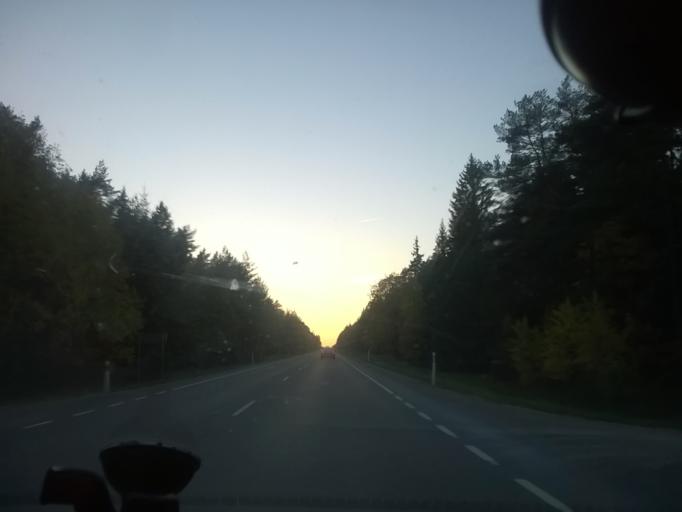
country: EE
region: Laeaene
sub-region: Lihula vald
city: Lihula
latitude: 58.9738
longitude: 23.9211
